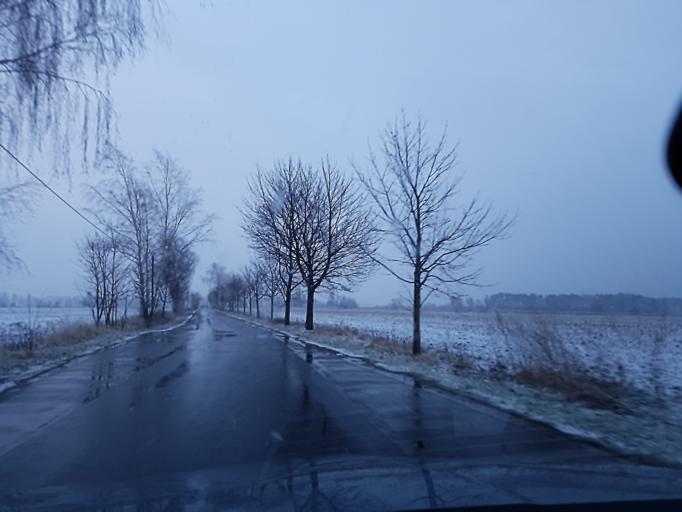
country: DE
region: Brandenburg
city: Elsterwerda
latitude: 51.4452
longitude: 13.5424
